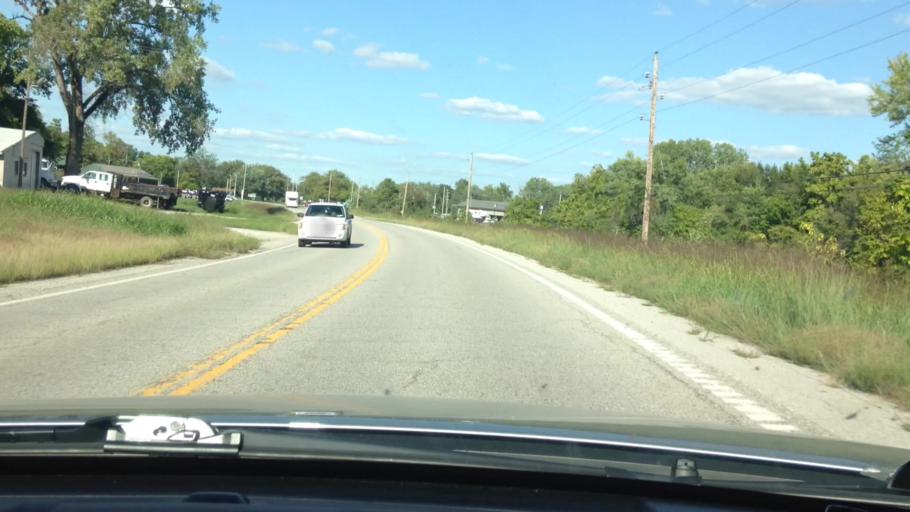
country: US
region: Missouri
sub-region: Platte County
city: Platte City
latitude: 39.3742
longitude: -94.7959
